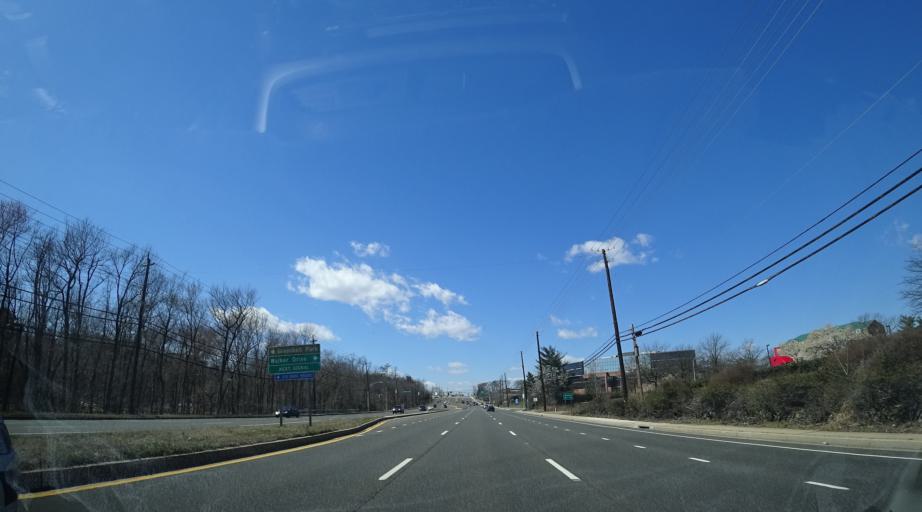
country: US
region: Maryland
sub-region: Prince George's County
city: Berwyn Heights
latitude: 38.9962
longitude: -76.8933
